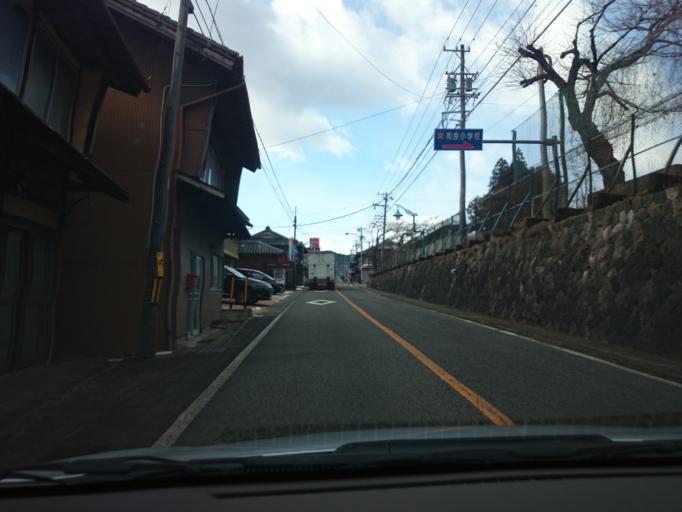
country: JP
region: Gifu
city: Gujo
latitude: 35.7461
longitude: 137.0806
